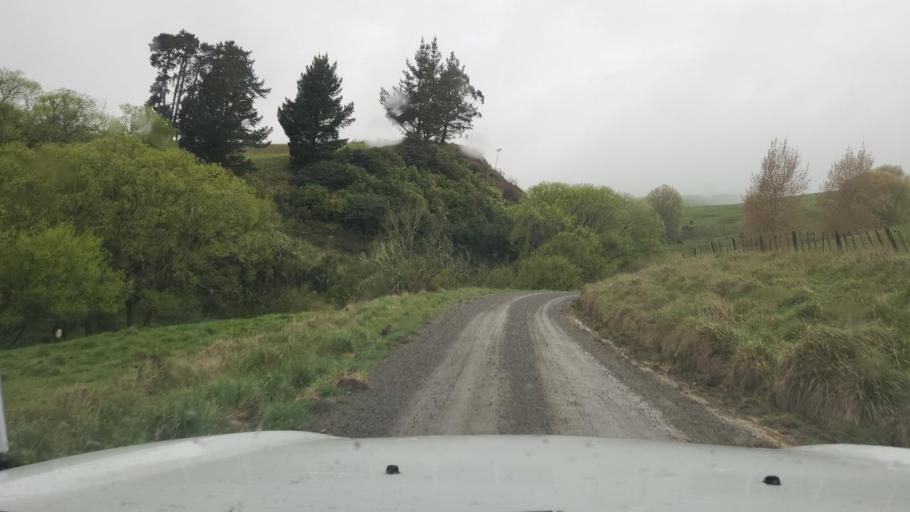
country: NZ
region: Wellington
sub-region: Masterton District
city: Masterton
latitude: -41.0857
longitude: 175.7244
